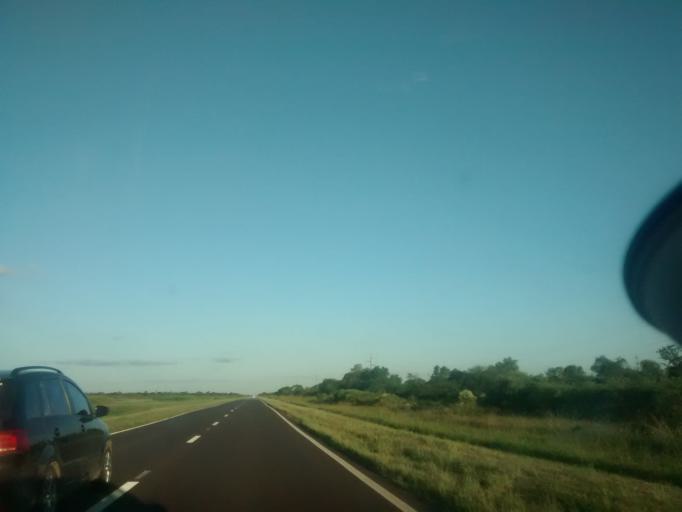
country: AR
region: Chaco
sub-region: Departamento de Presidencia de la Plaza
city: Presidencia de la Plaza
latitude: -27.0206
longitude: -59.8114
